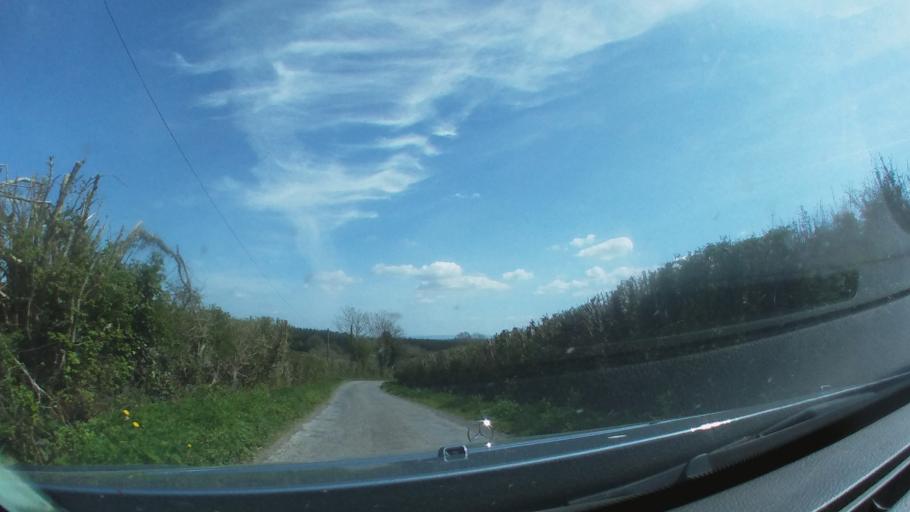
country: IE
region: Leinster
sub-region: Kilkenny
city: Callan
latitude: 52.6213
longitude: -7.5064
